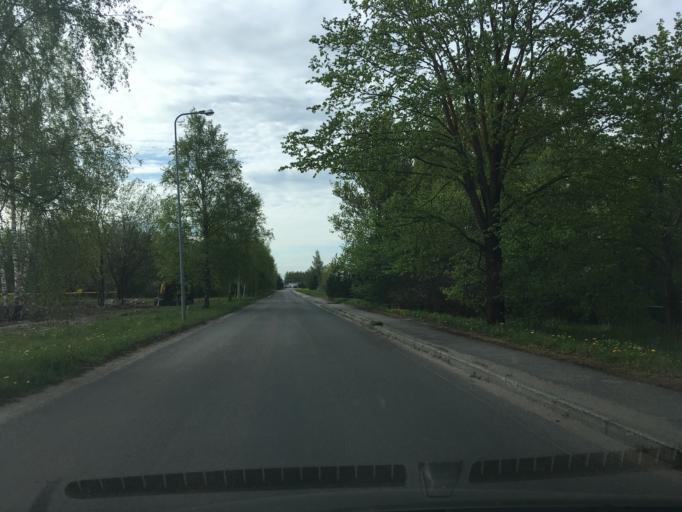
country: EE
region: Harju
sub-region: Tallinna linn
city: Kose
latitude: 59.4308
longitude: 24.8526
